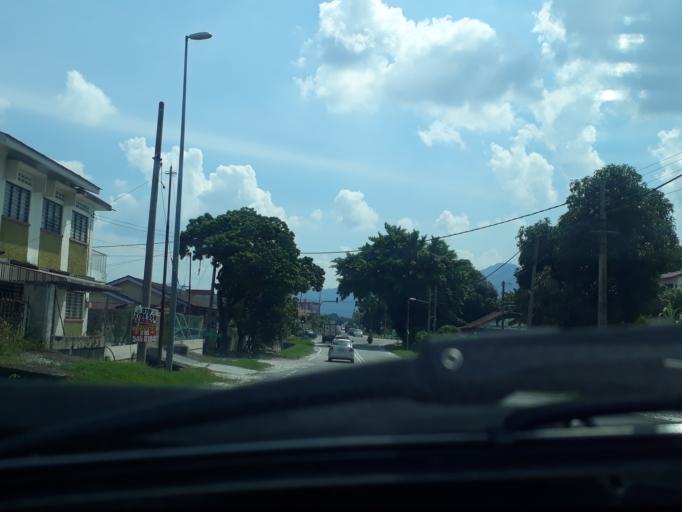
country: MY
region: Perak
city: Ipoh
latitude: 4.5774
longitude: 101.0862
